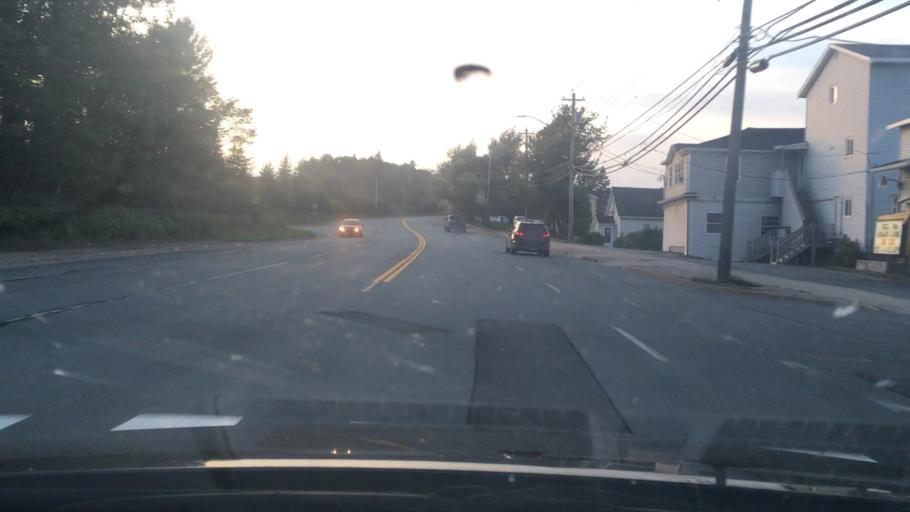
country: CA
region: Nova Scotia
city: Halifax
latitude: 44.6362
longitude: -63.5273
